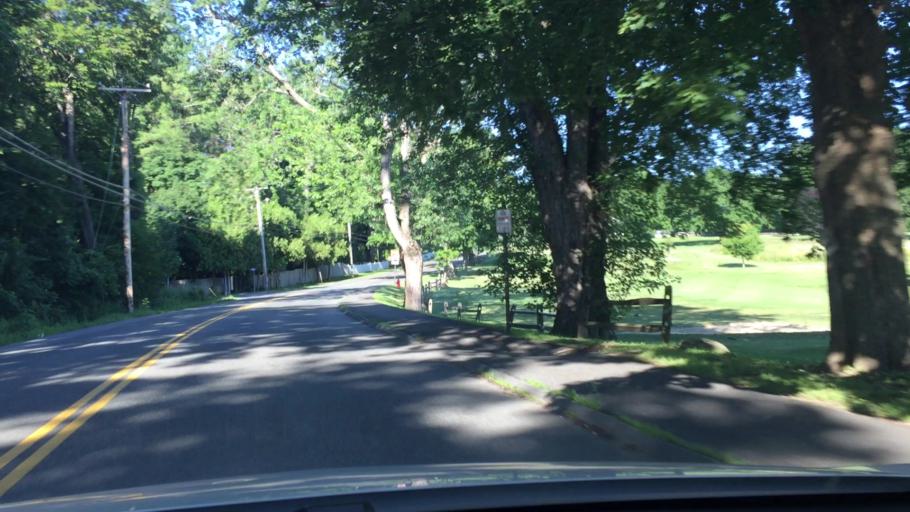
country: US
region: Massachusetts
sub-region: Berkshire County
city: Lee
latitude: 42.3021
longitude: -73.2567
